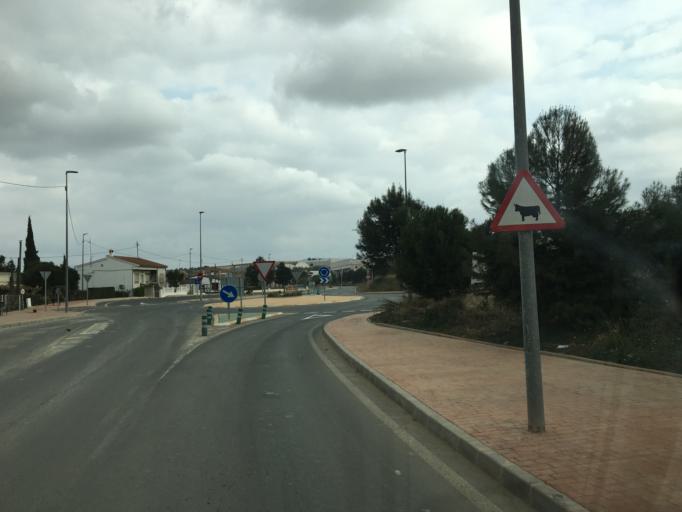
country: ES
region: Murcia
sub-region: Murcia
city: Beniel
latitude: 38.0195
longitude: -0.9841
